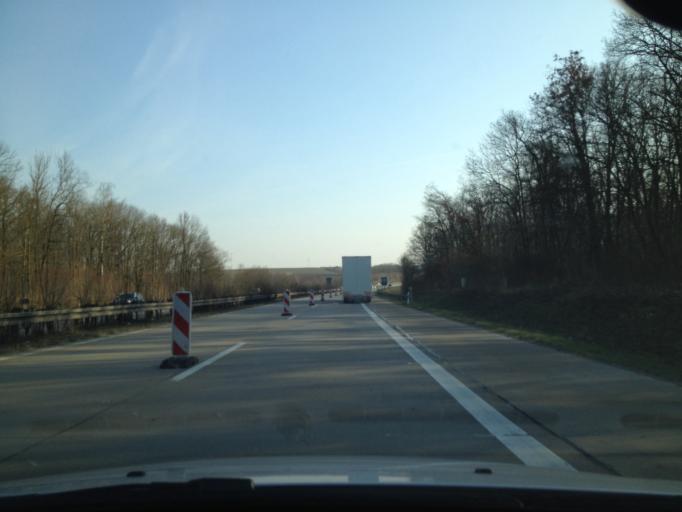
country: DE
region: Bavaria
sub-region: Regierungsbezirk Mittelfranken
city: Gollhofen
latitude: 49.5745
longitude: 10.1724
